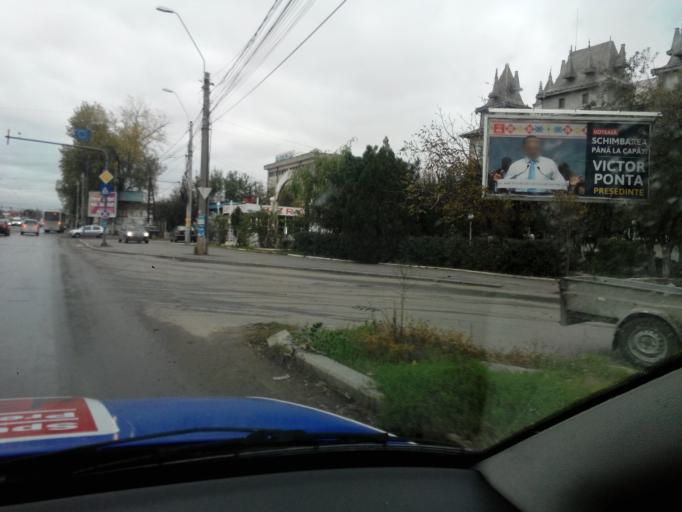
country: RO
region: Ilfov
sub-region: Comuna Jilava
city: Jilava
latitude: 44.3684
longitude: 26.0891
